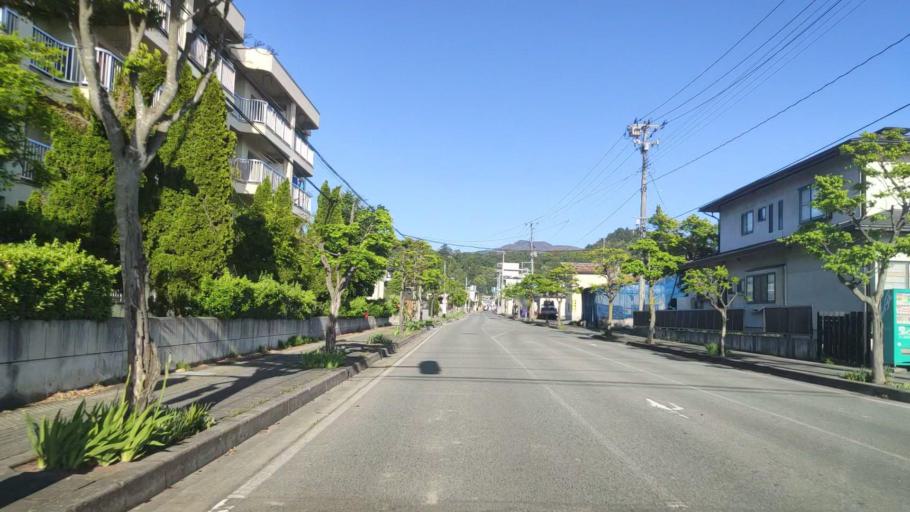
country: JP
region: Yamagata
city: Tendo
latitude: 38.3550
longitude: 140.3649
